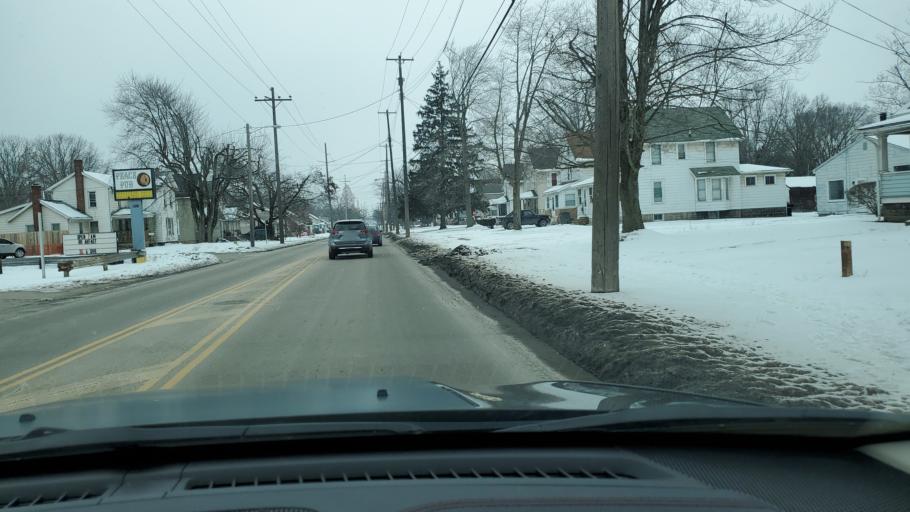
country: US
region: Ohio
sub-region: Trumbull County
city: Warren
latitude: 41.2416
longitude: -80.8376
